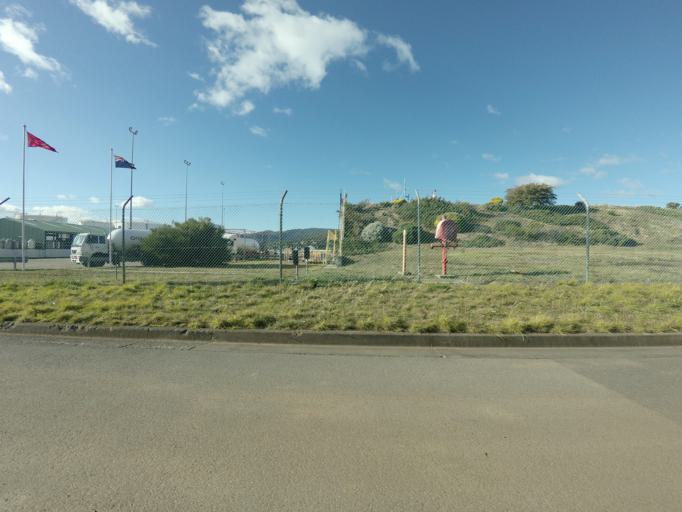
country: AU
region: Tasmania
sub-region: Hobart
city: New Town
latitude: -42.8482
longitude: 147.3257
